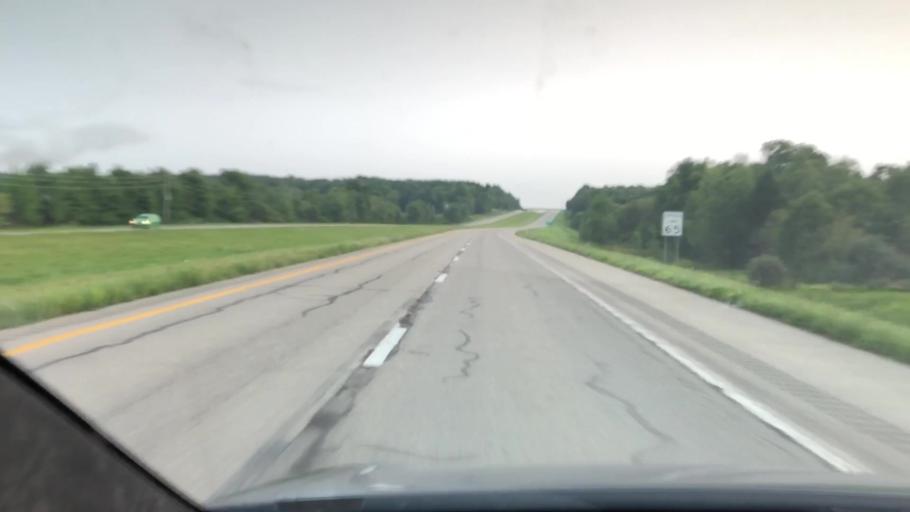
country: US
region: Pennsylvania
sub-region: Venango County
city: Sugarcreek
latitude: 41.2590
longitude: -79.9321
